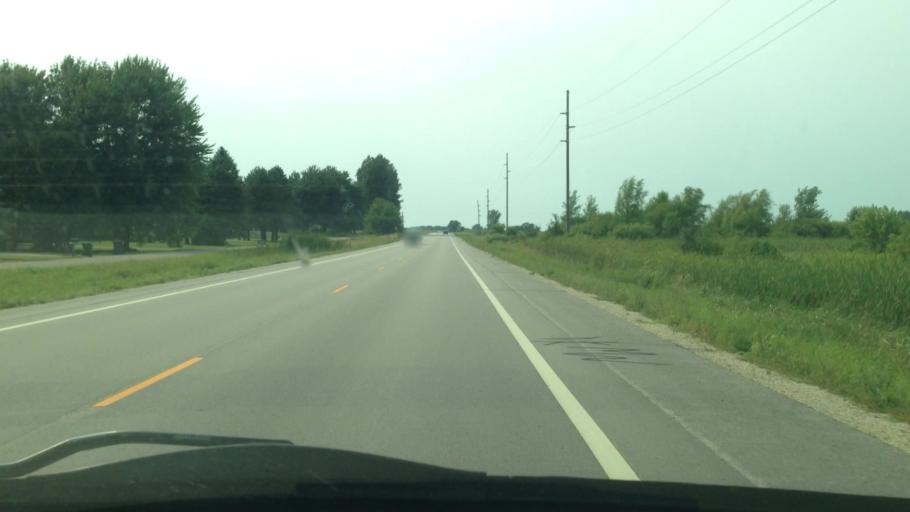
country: US
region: Minnesota
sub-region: Olmsted County
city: Eyota
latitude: 43.9944
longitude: -92.2350
